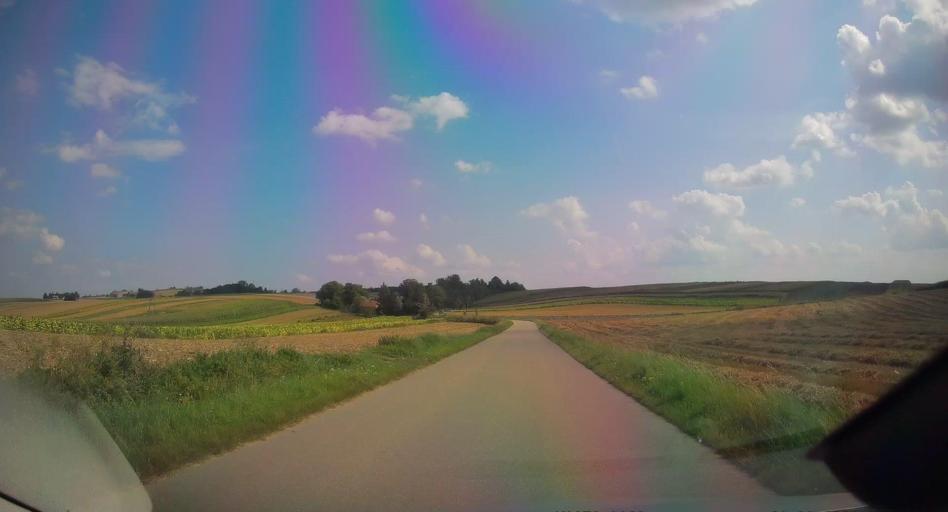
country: PL
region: Lesser Poland Voivodeship
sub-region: Powiat bochenski
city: Dziewin
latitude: 50.1585
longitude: 20.4583
